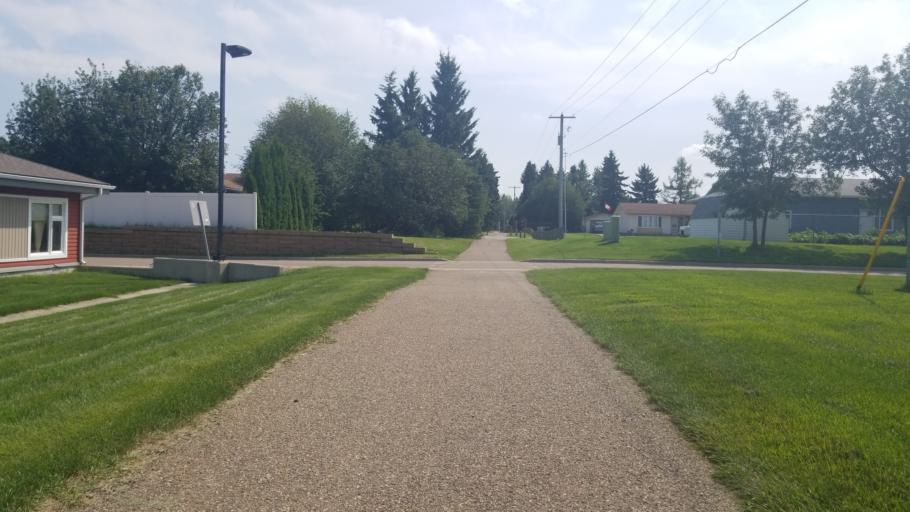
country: CA
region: Saskatchewan
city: Lloydminster
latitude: 53.2737
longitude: -110.0176
